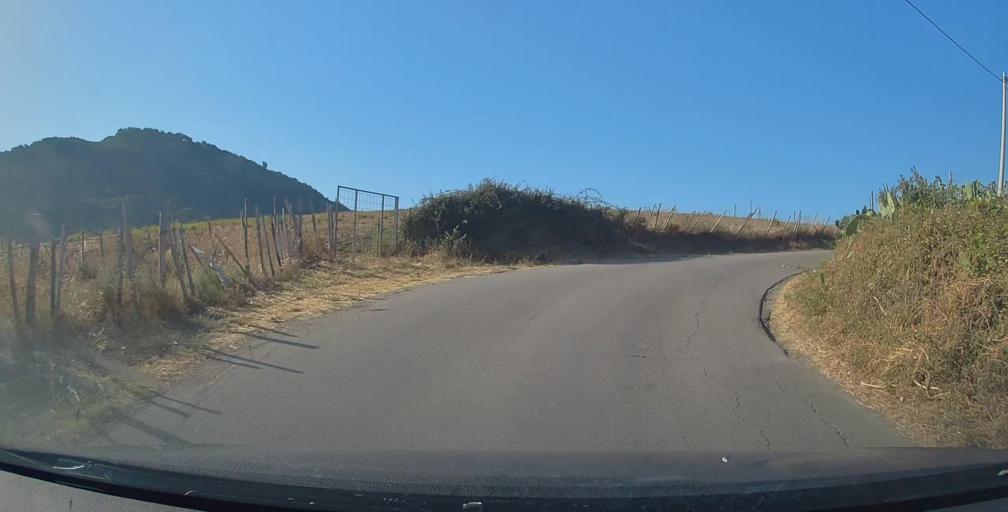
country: IT
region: Sicily
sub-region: Messina
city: San Piero Patti
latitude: 38.0699
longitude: 14.9866
